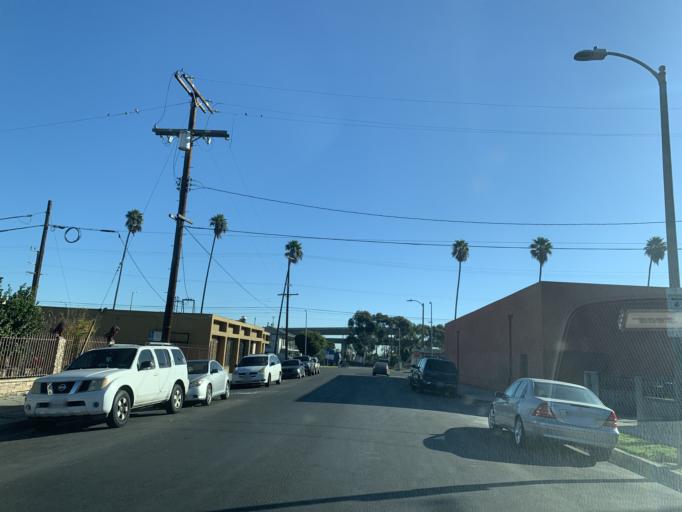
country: US
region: California
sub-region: Los Angeles County
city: Westmont
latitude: 33.9320
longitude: -118.2834
